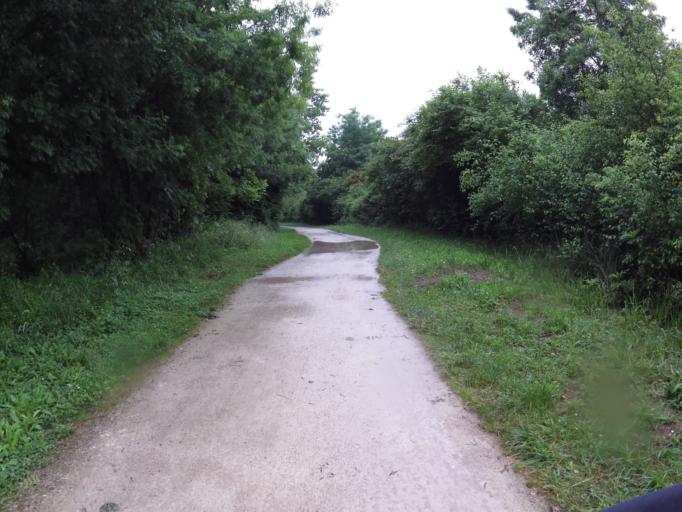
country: FR
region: Poitou-Charentes
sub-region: Departement de la Charente
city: Angouleme
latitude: 45.6643
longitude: 0.1592
